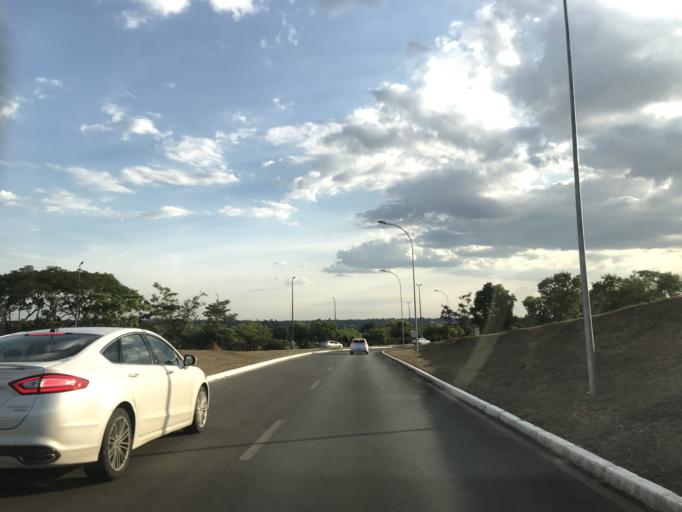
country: BR
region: Federal District
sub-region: Brasilia
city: Brasilia
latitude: -15.8189
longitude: -47.8812
